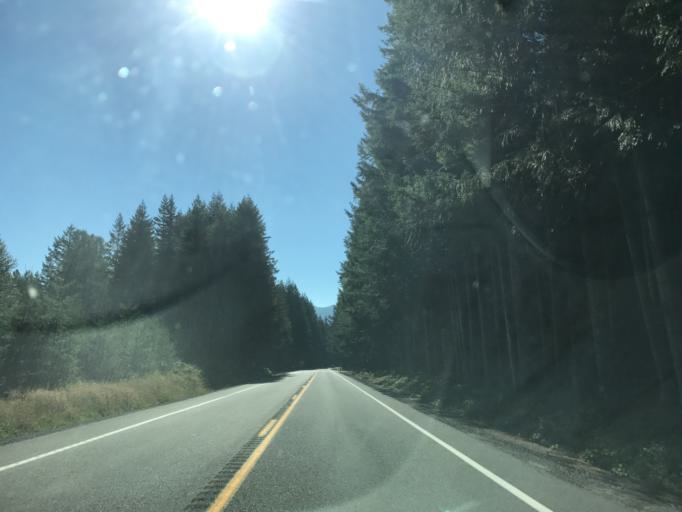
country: US
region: Washington
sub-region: King County
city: Riverbend
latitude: 47.1388
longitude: -121.6275
